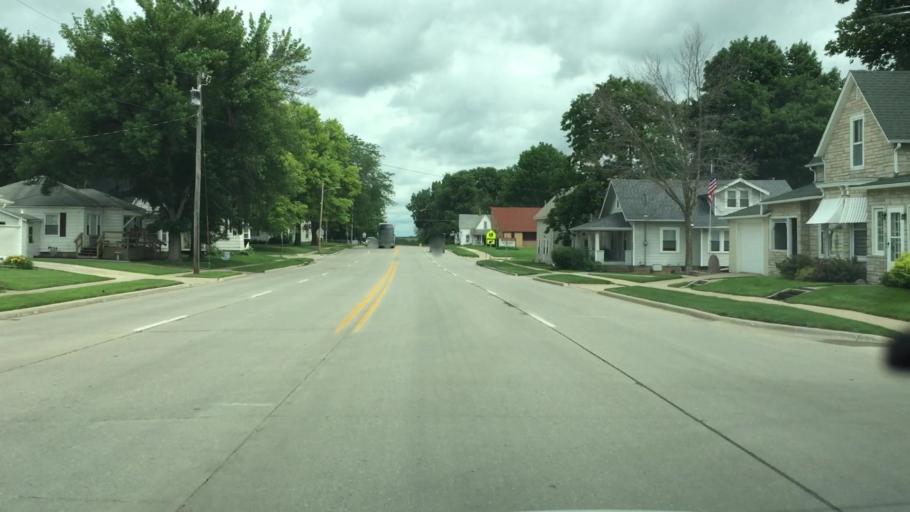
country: US
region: Iowa
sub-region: Jasper County
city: Monroe
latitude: 41.5233
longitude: -93.1018
